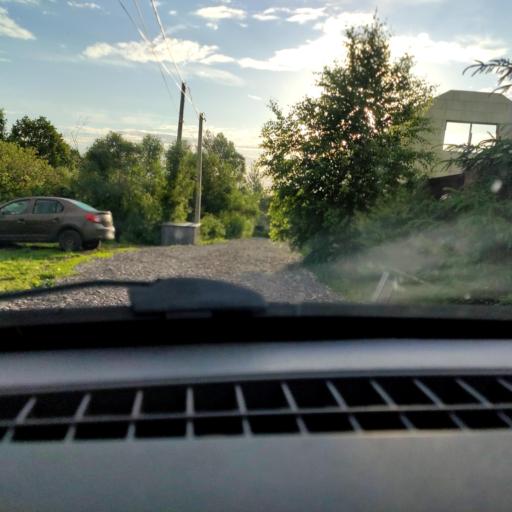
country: RU
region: Bashkortostan
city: Mikhaylovka
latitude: 54.7393
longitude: 55.8267
